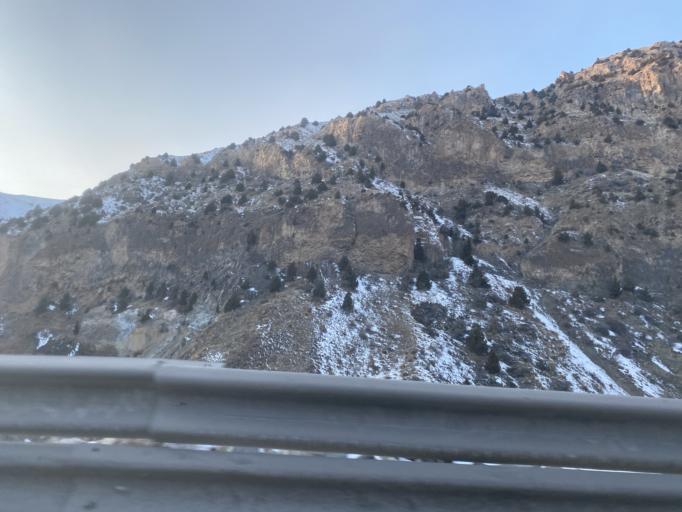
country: IR
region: Tehran
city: Damavand
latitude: 35.8572
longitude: 52.0892
